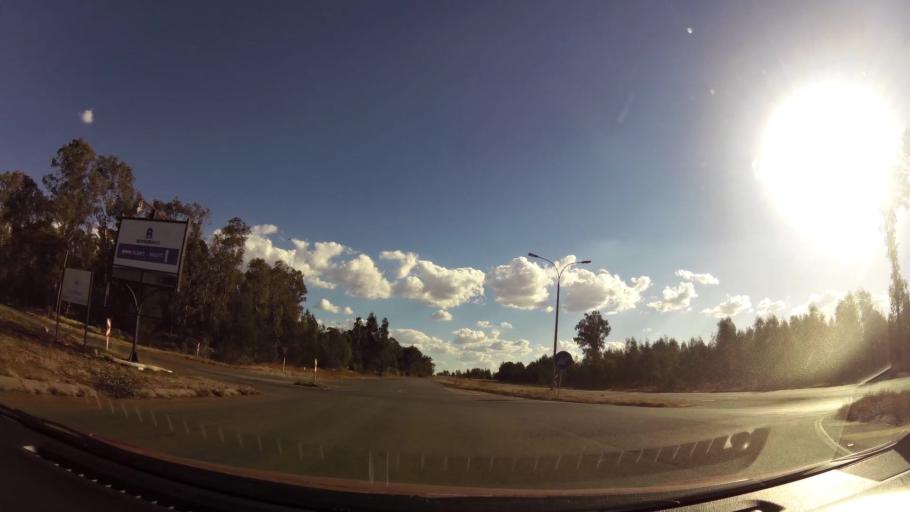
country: ZA
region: Gauteng
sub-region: West Rand District Municipality
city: Carletonville
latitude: -26.3773
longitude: 27.3936
